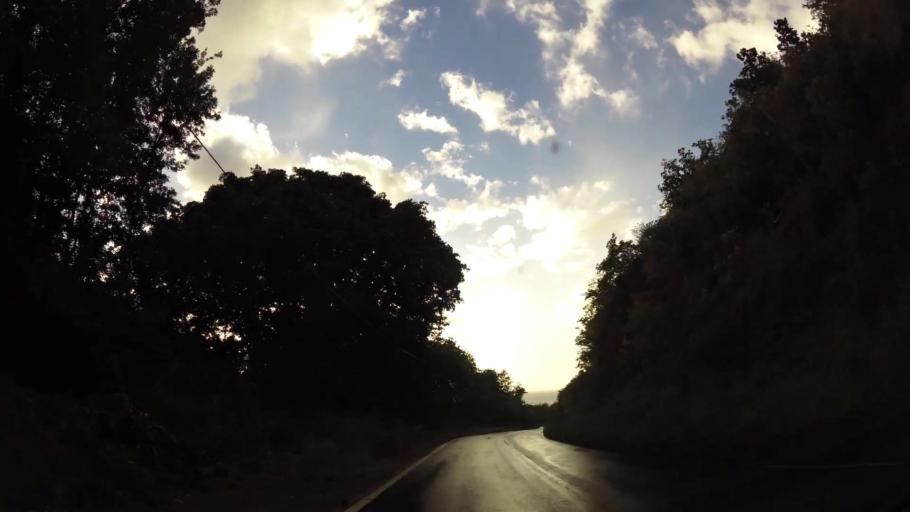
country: DM
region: Saint Peter
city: Colihaut
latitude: 15.5313
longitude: -61.4715
